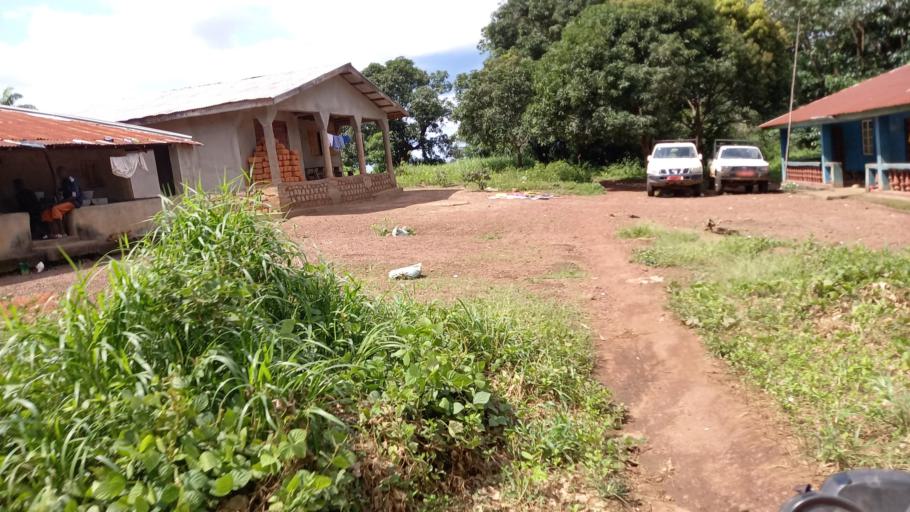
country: SL
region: Northern Province
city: Kamakwie
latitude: 9.5138
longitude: -12.2413
